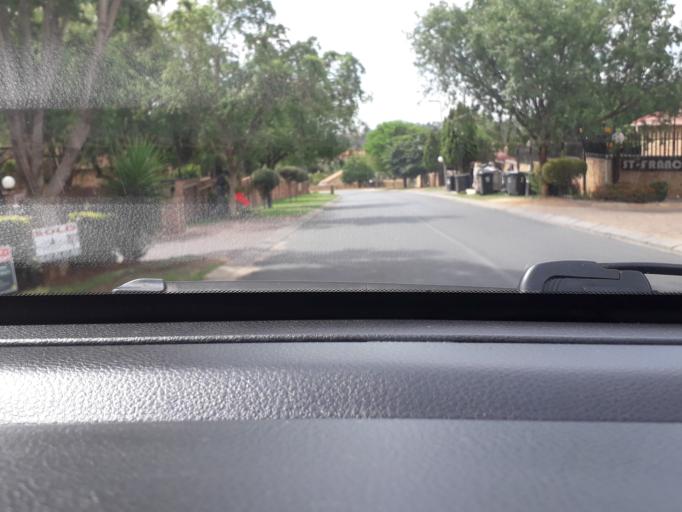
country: ZA
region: Gauteng
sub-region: City of Johannesburg Metropolitan Municipality
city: Roodepoort
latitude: -26.1019
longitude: 27.9001
